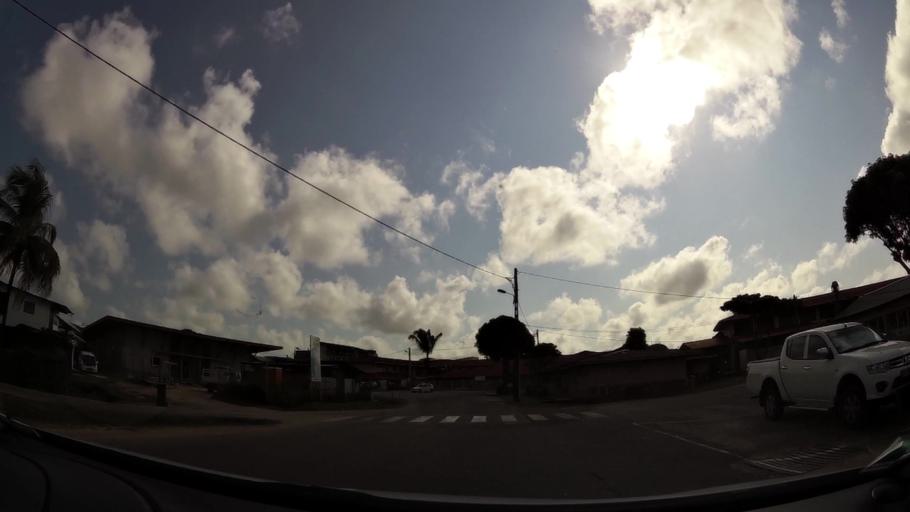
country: GF
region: Guyane
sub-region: Guyane
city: Cayenne
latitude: 4.9327
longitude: -52.3251
